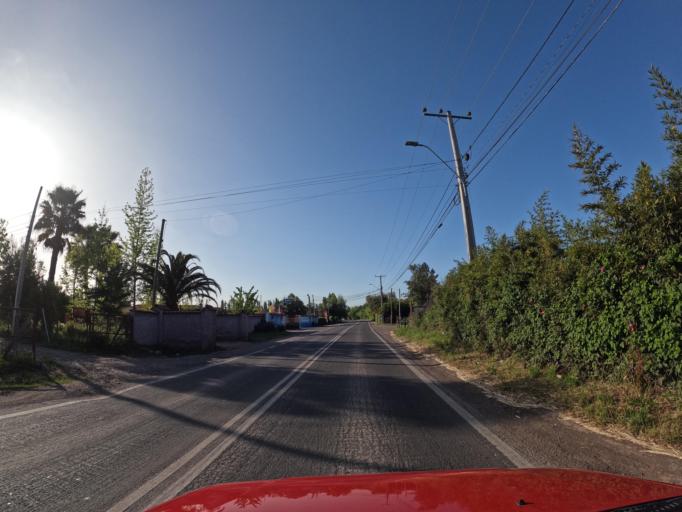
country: CL
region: O'Higgins
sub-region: Provincia de Colchagua
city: Santa Cruz
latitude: -34.6617
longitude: -71.3396
